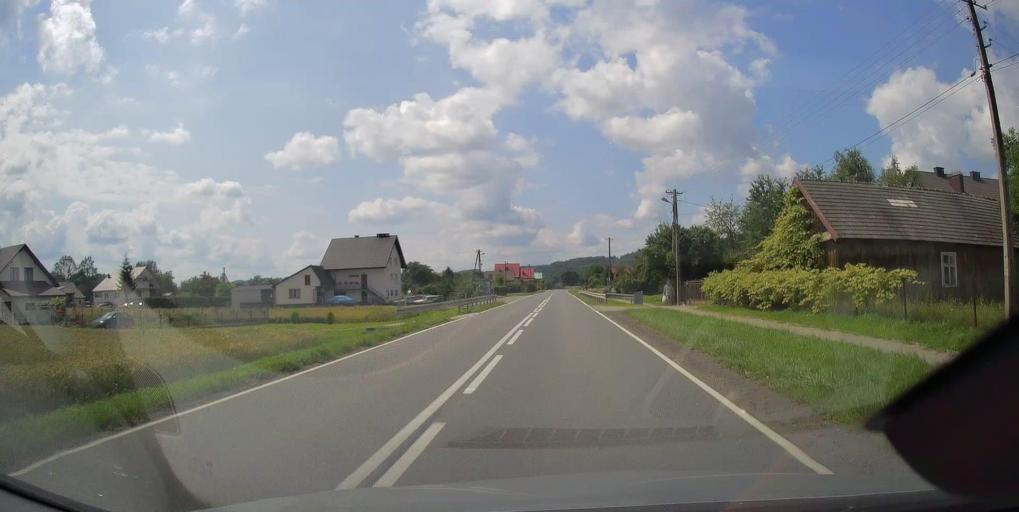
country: PL
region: Lesser Poland Voivodeship
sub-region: Powiat tarnowski
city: Wielka Wies
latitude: 49.9080
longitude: 20.8187
